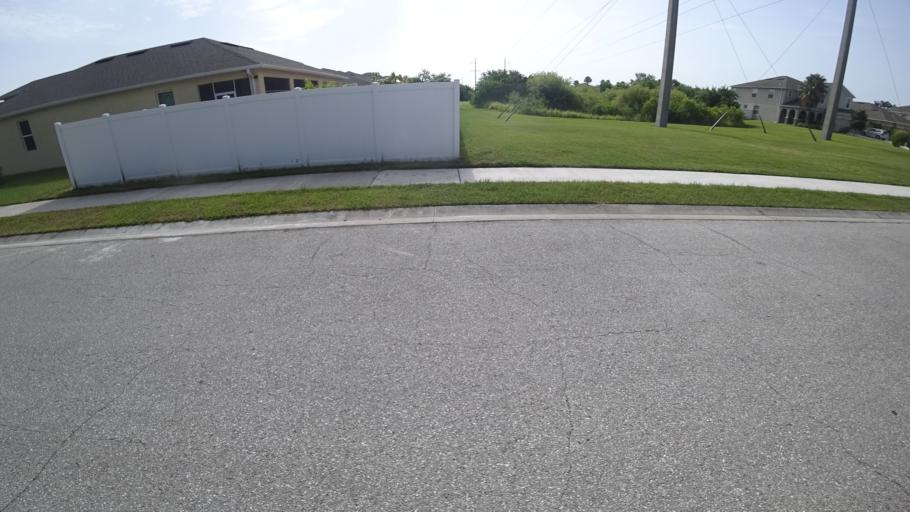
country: US
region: Florida
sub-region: Manatee County
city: Ellenton
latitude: 27.5524
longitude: -82.5074
